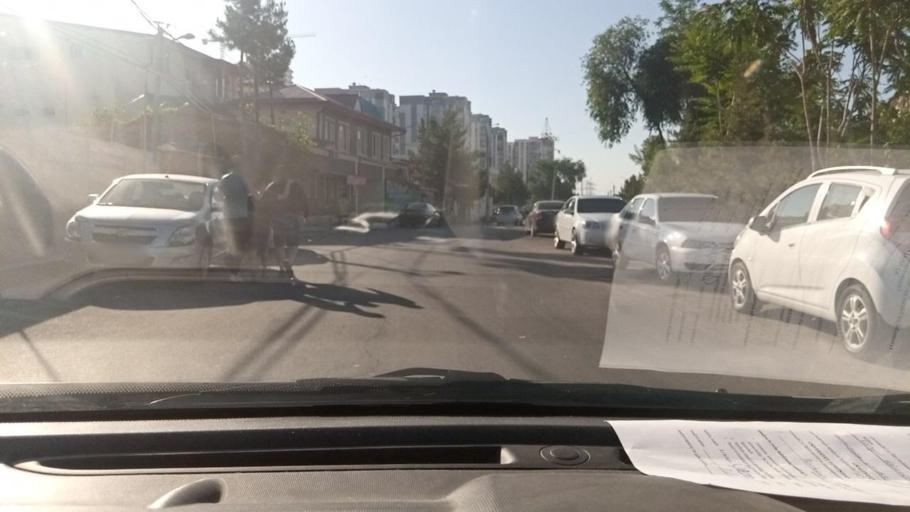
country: UZ
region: Toshkent
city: Salor
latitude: 41.3242
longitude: 69.3561
